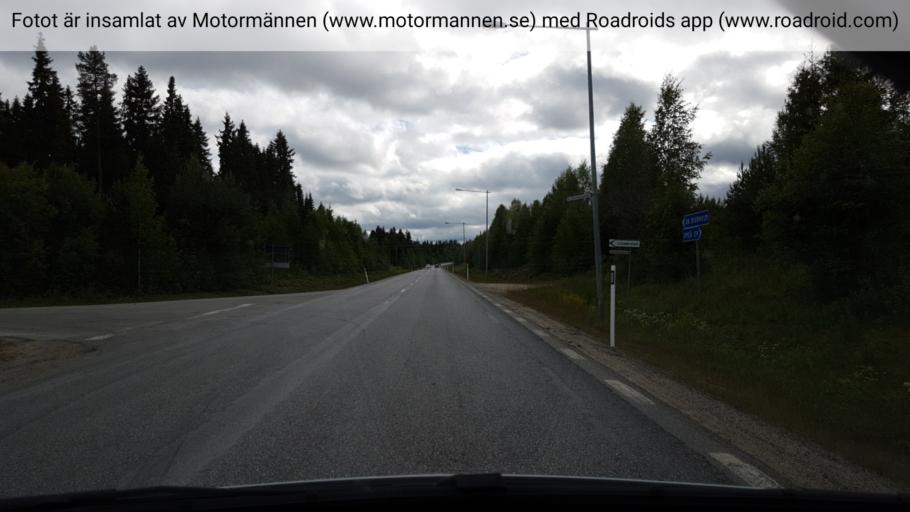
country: SE
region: Vaesterbotten
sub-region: Vannas Kommun
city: Vaennaes
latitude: 63.9190
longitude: 19.7385
